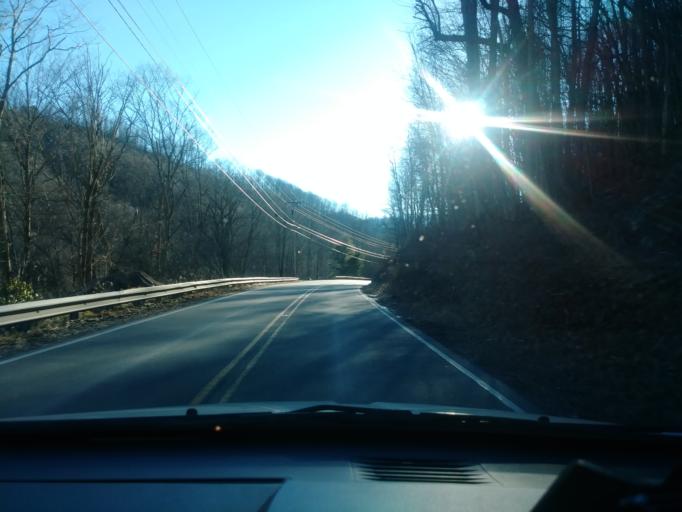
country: US
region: North Carolina
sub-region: Avery County
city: Banner Elk
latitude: 36.1759
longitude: -81.9288
